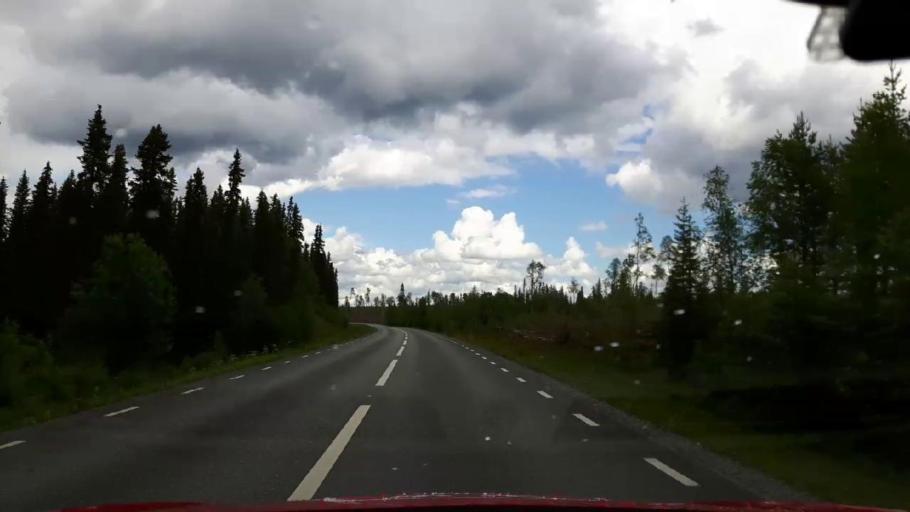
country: SE
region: Jaemtland
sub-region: Krokoms Kommun
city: Krokom
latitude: 63.7756
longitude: 14.3458
